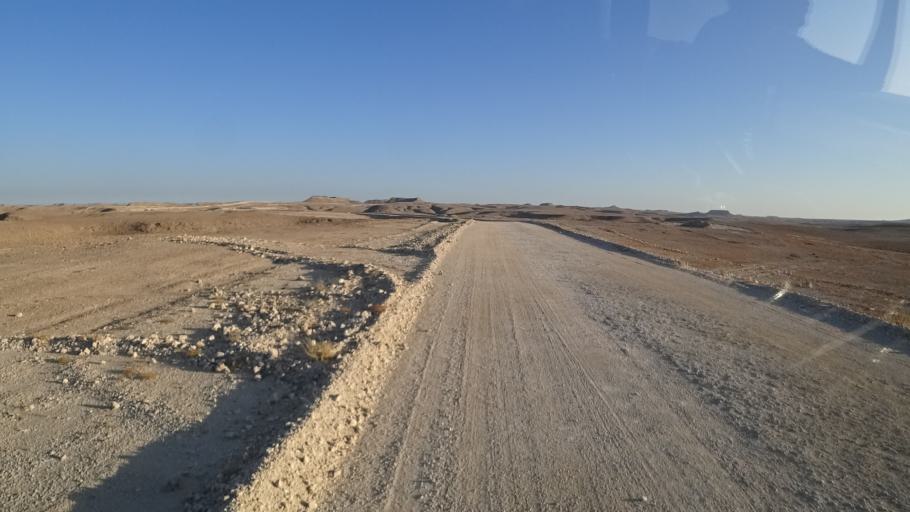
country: YE
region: Al Mahrah
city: Hawf
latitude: 17.1563
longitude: 53.3499
